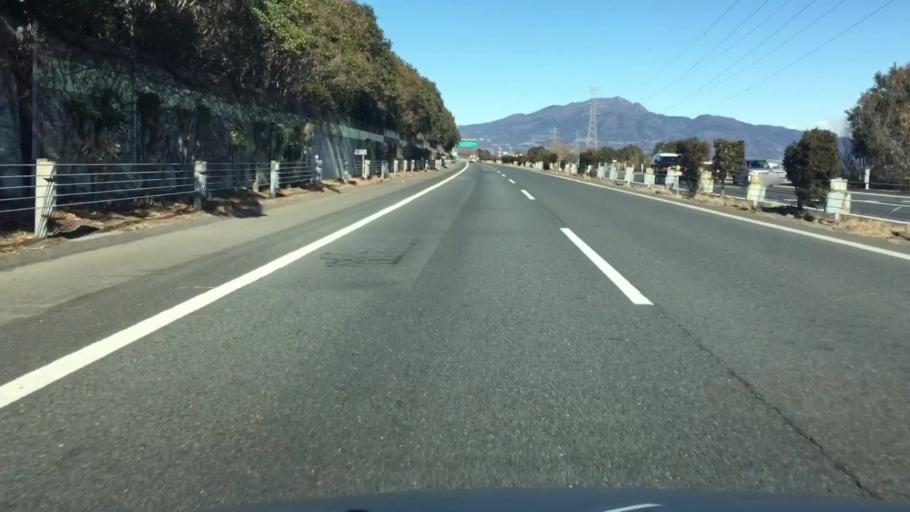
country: JP
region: Gunma
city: Shibukawa
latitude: 36.4545
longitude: 139.0139
